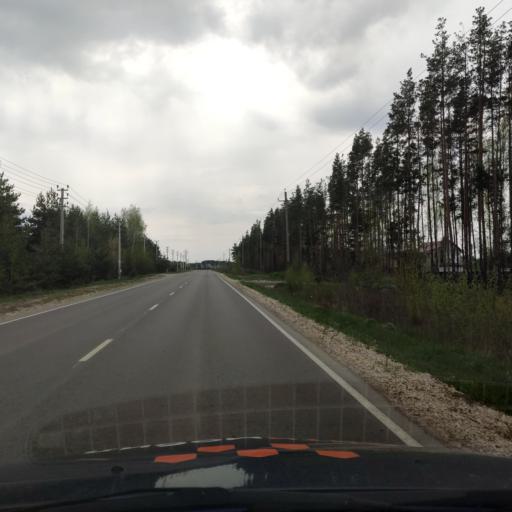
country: RU
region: Voronezj
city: Podgornoye
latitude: 51.8607
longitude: 39.1655
